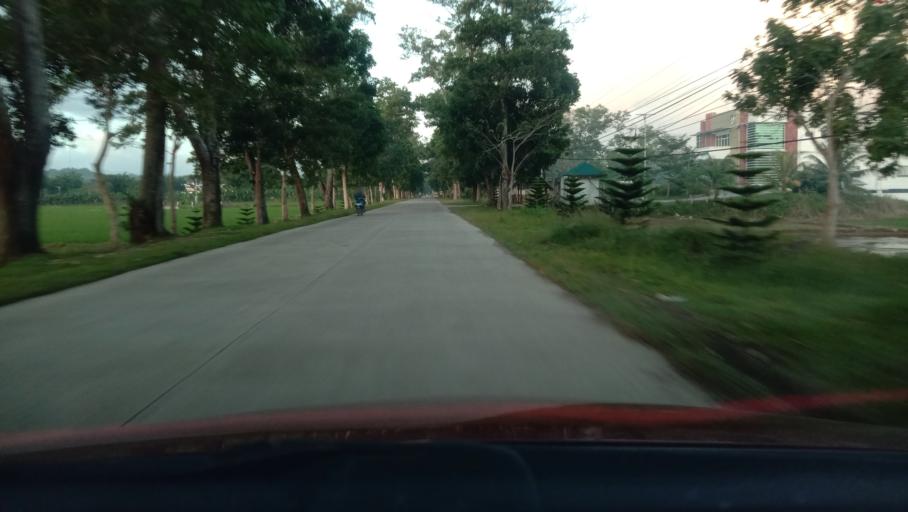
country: PH
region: Caraga
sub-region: Province of Agusan del Sur
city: Patin-ay
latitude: 8.5484
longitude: 125.9429
